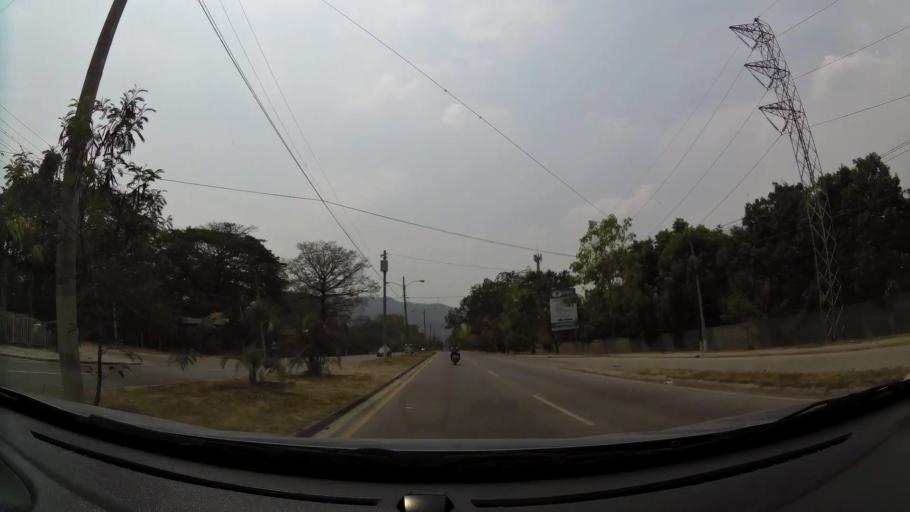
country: HN
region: Cortes
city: Nuevo Chamelecon
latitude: 15.4037
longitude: -88.0042
